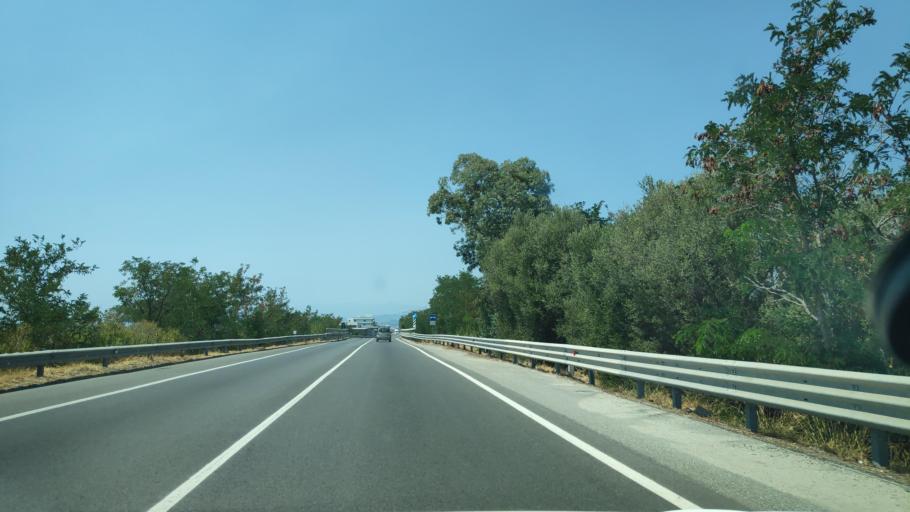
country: IT
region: Calabria
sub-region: Provincia di Reggio Calabria
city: Roccella Ionica
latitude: 38.3091
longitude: 16.3674
